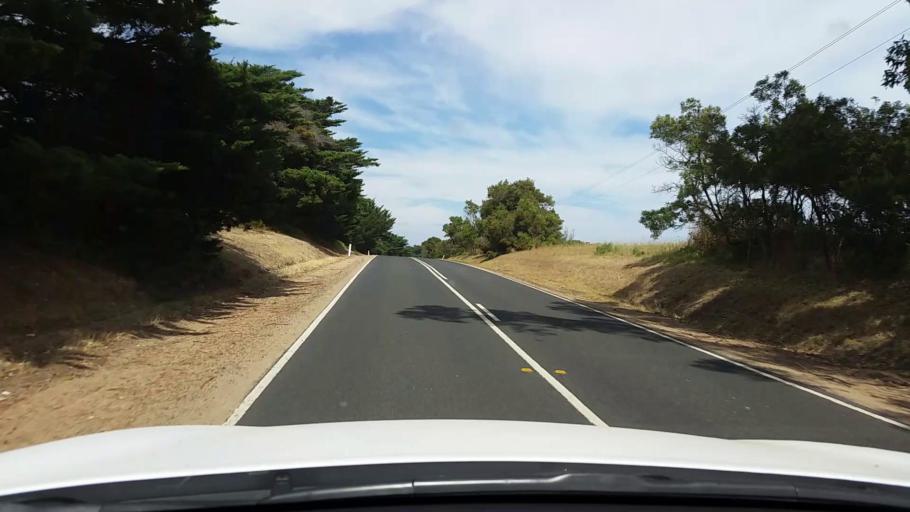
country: AU
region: Victoria
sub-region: Mornington Peninsula
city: Merricks
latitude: -38.4767
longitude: 144.9944
